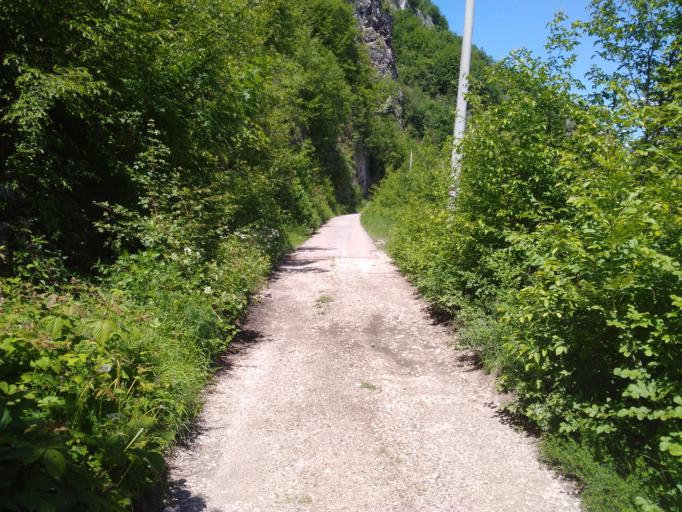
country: BA
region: Federation of Bosnia and Herzegovina
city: Kobilja Glava
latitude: 43.8507
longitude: 18.4577
